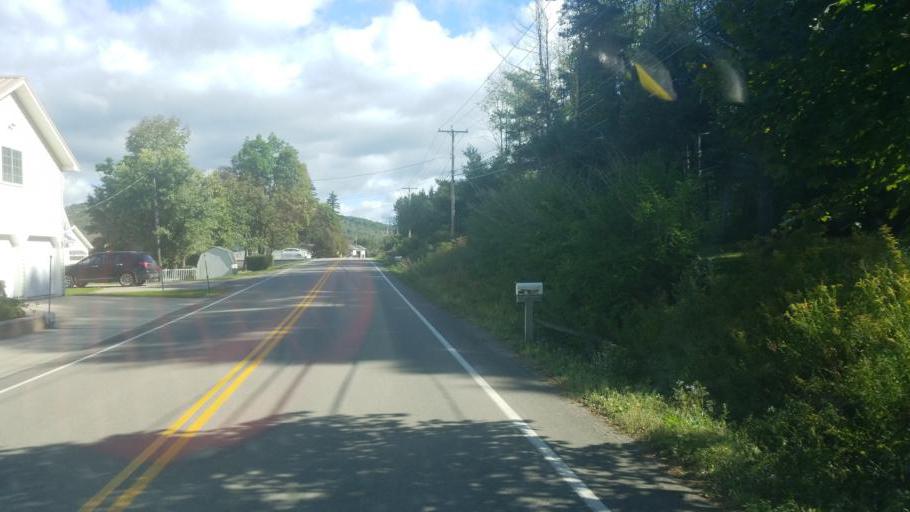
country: US
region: New York
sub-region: Allegany County
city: Cuba
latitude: 42.2450
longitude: -78.2981
